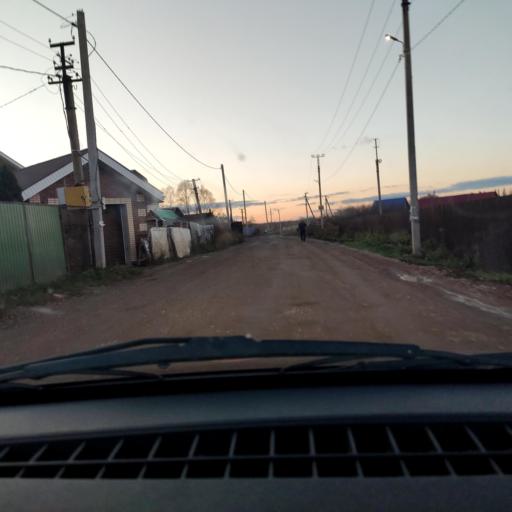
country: RU
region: Bashkortostan
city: Ufa
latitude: 54.6413
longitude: 55.9176
